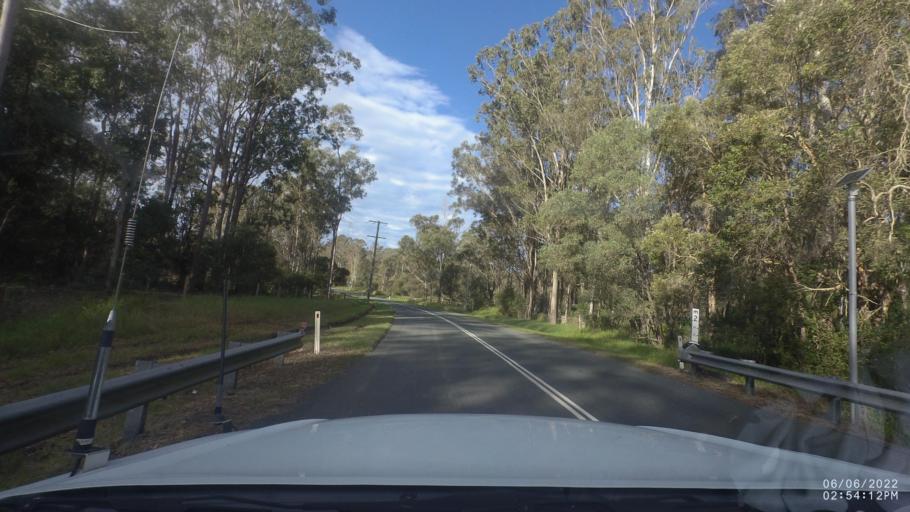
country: AU
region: Queensland
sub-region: Logan
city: Cedar Vale
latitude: -27.8553
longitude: 153.0469
